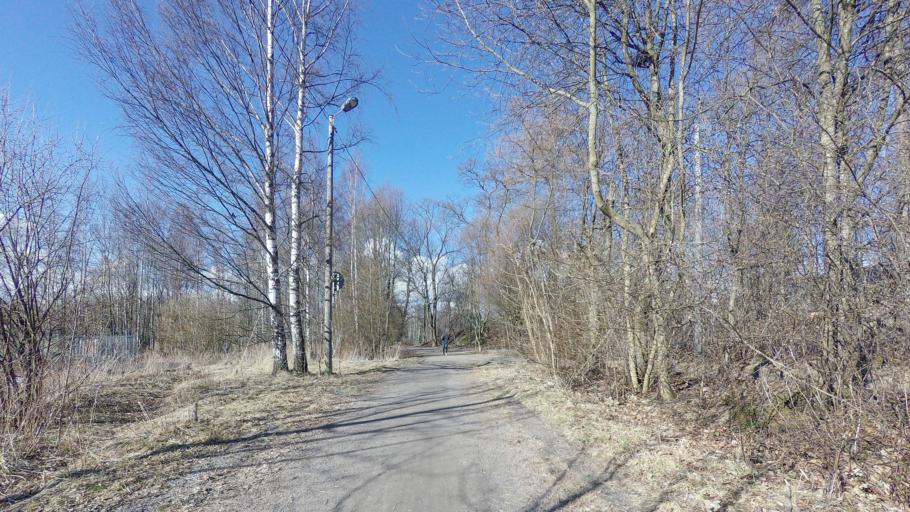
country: FI
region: Uusimaa
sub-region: Helsinki
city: Vantaa
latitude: 60.1747
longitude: 25.0586
